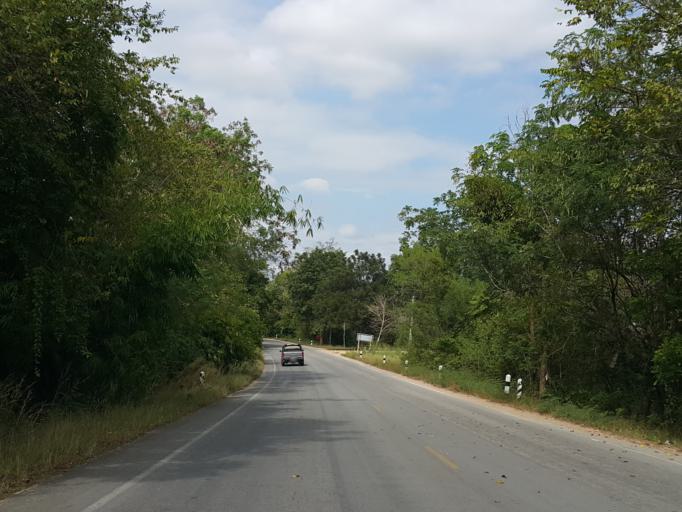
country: TH
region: Lampang
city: Lampang
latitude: 18.3925
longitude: 99.4573
